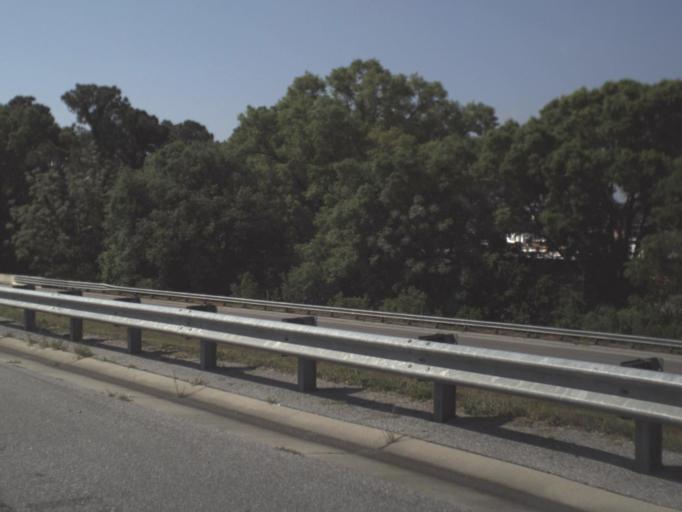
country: US
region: Florida
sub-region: Escambia County
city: Goulding
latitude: 30.4505
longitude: -87.2207
